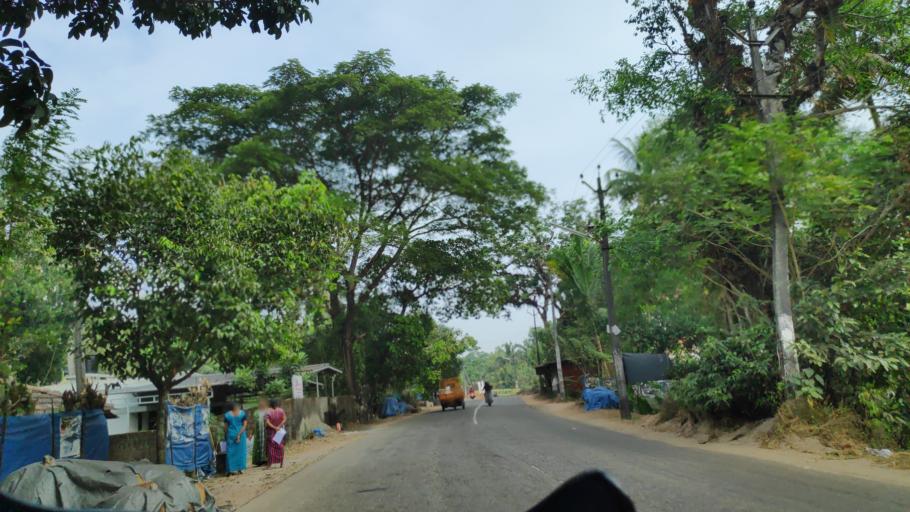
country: IN
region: Kerala
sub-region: Alappuzha
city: Vayalar
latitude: 9.7214
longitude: 76.3605
